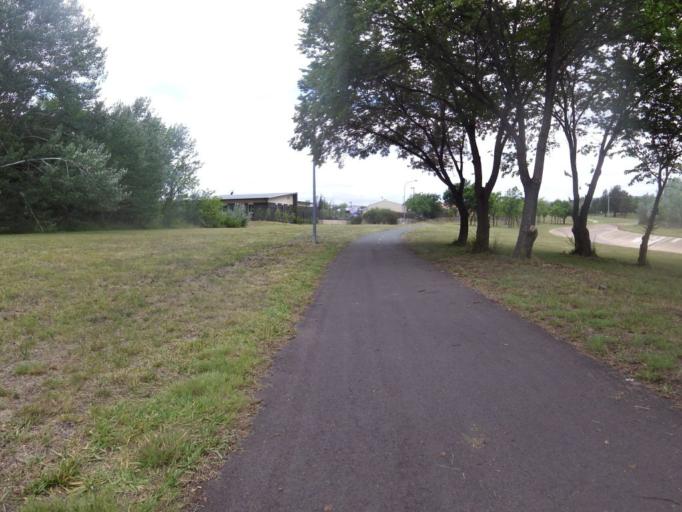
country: AU
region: Australian Capital Territory
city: Macarthur
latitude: -35.4201
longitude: 149.0920
